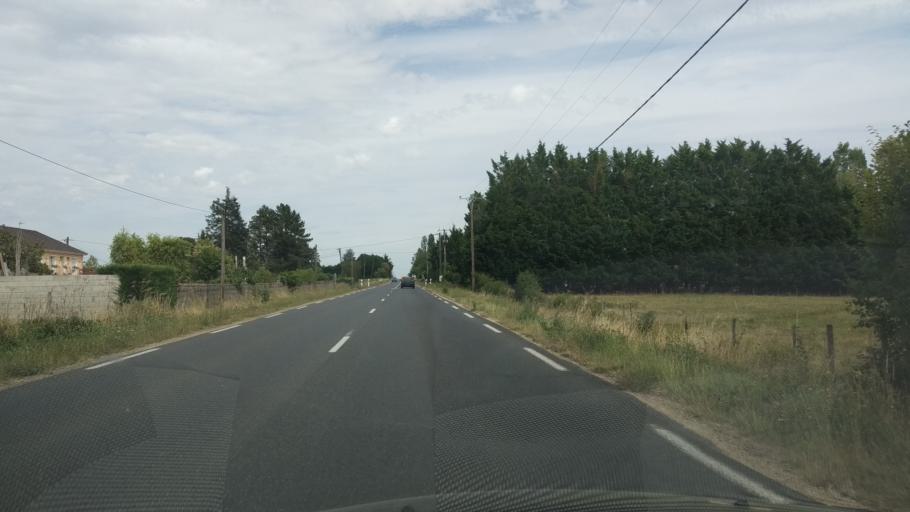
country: FR
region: Poitou-Charentes
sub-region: Departement de la Vienne
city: Mignaloux-Beauvoir
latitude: 46.5613
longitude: 0.4336
